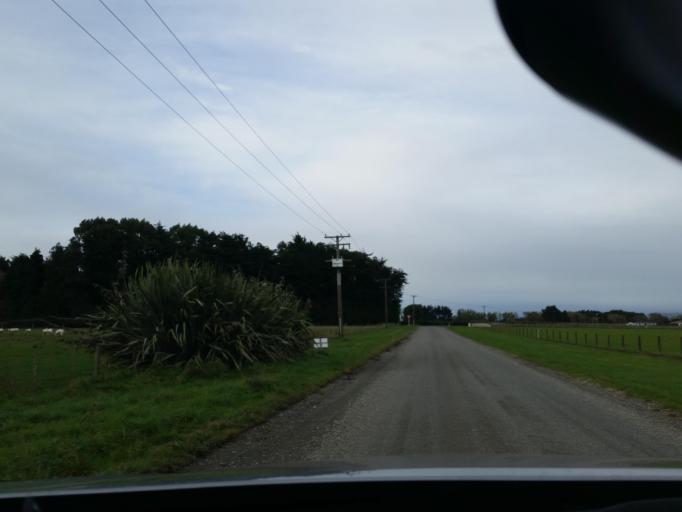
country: NZ
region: Southland
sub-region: Invercargill City
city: Invercargill
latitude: -46.3078
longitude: 168.3033
